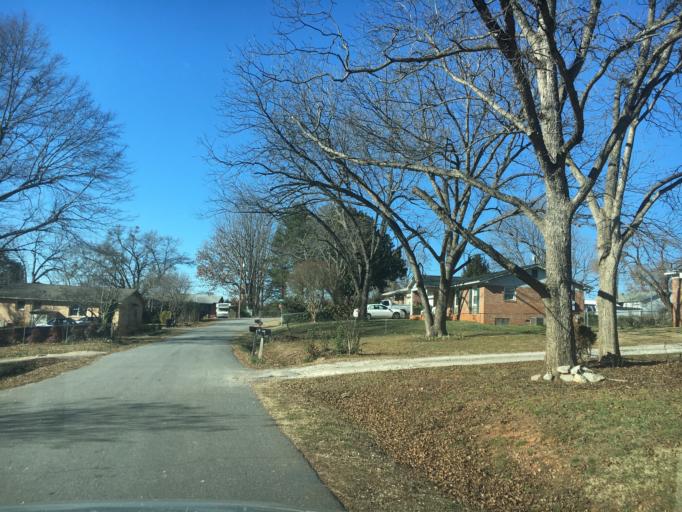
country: US
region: South Carolina
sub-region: Spartanburg County
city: Duncan
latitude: 34.9515
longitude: -82.1659
